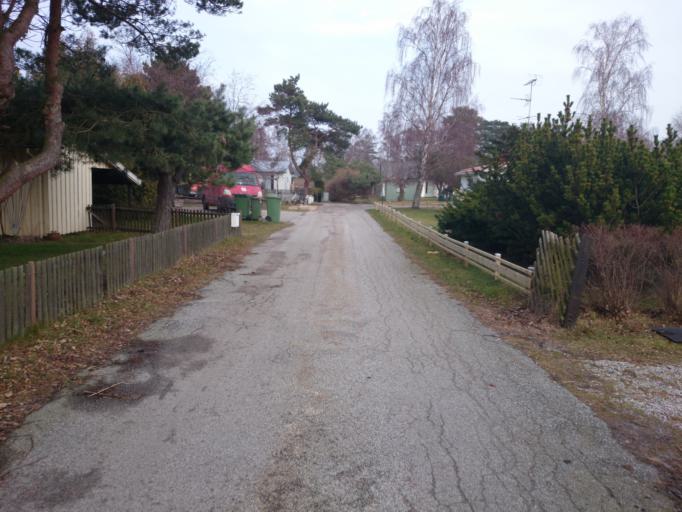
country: SE
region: Skane
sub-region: Vellinge Kommun
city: Skanor med Falsterbo
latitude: 55.3957
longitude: 12.8553
